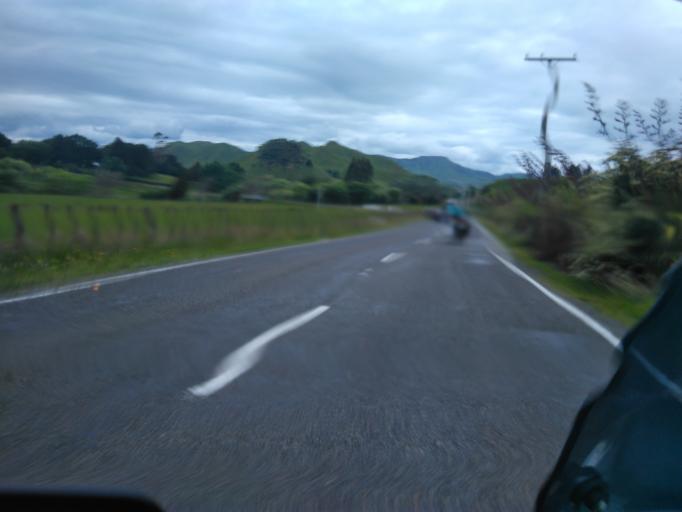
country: NZ
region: Bay of Plenty
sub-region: Opotiki District
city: Opotiki
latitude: -38.3628
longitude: 177.4955
